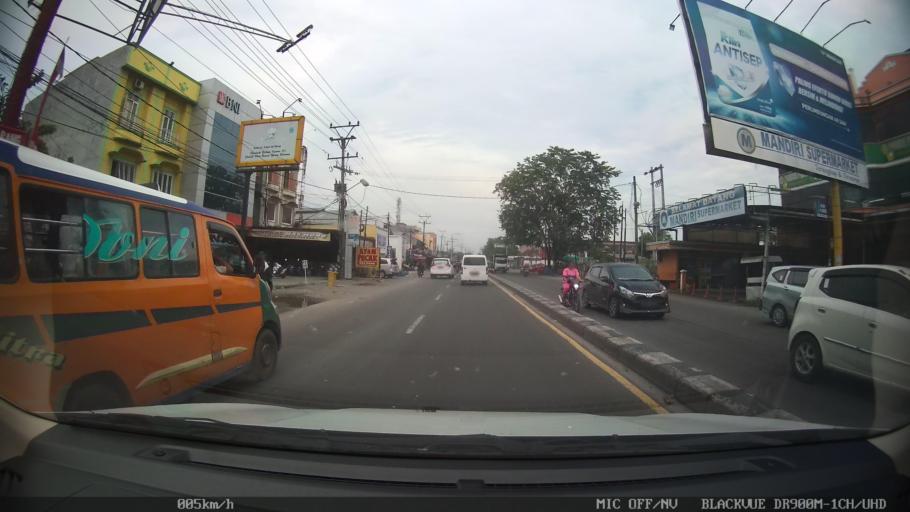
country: ID
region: North Sumatra
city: Sunggal
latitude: 3.5995
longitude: 98.5748
